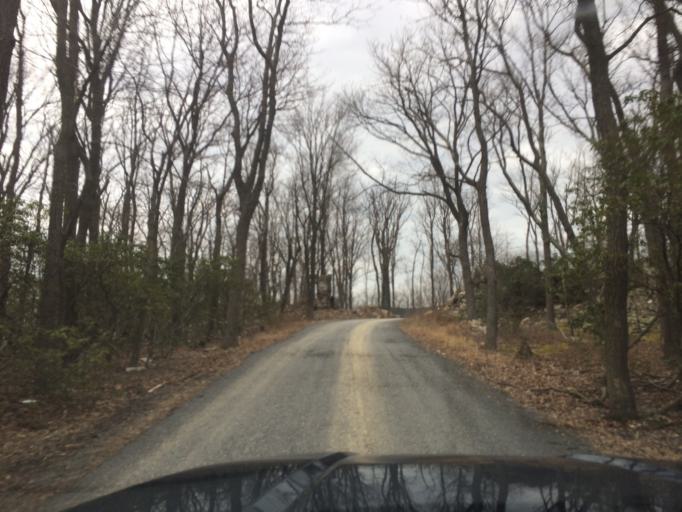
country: US
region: Maryland
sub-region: Frederick County
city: Braddock Heights
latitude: 39.4497
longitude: -77.4871
